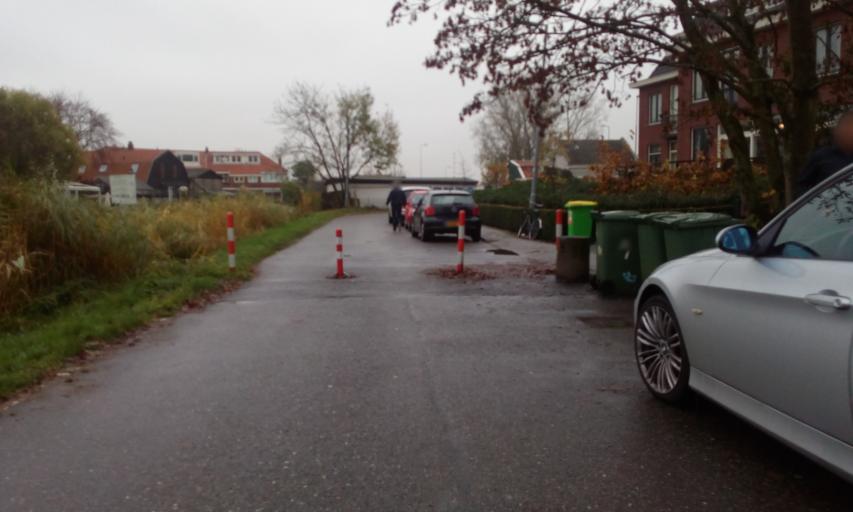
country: NL
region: South Holland
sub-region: Gemeente Lansingerland
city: Bergschenhoek
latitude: 51.9563
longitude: 4.5174
